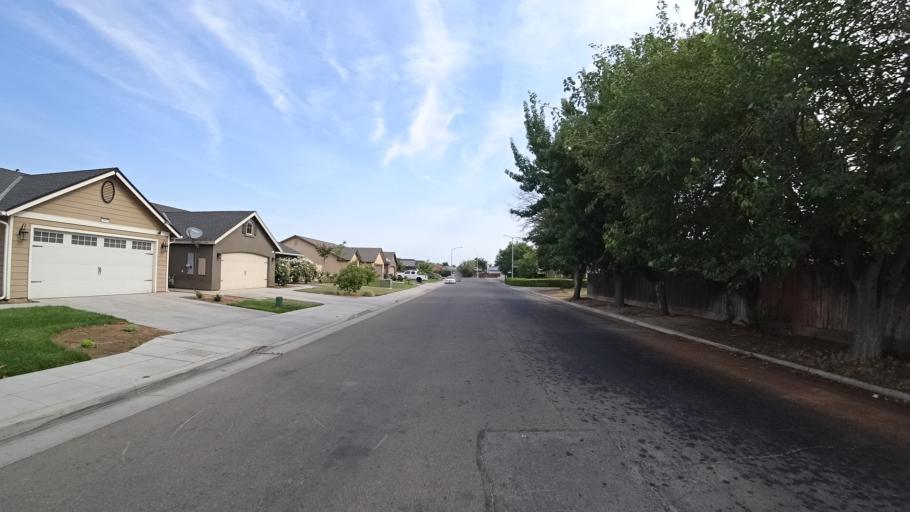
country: US
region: California
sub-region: Fresno County
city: West Park
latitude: 36.7729
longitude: -119.8758
